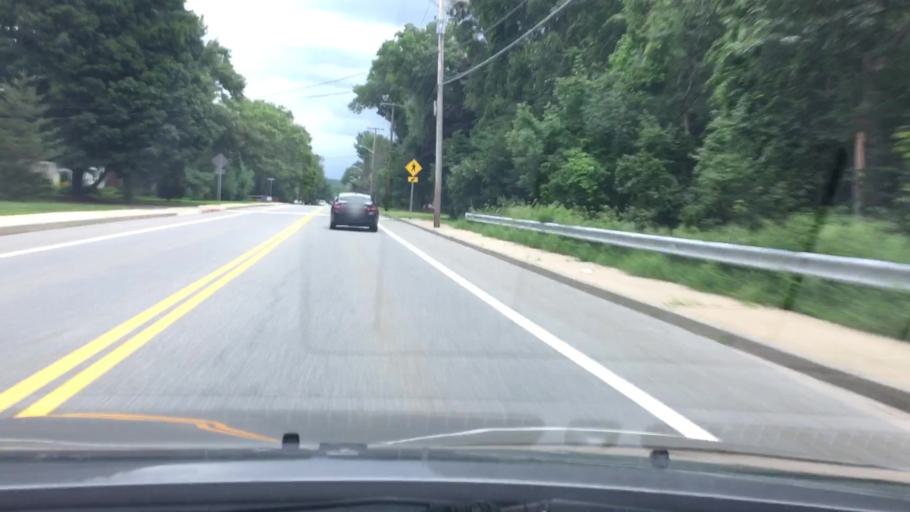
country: US
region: Rhode Island
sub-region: Providence County
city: Cumberland
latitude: 41.9813
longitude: -71.4030
